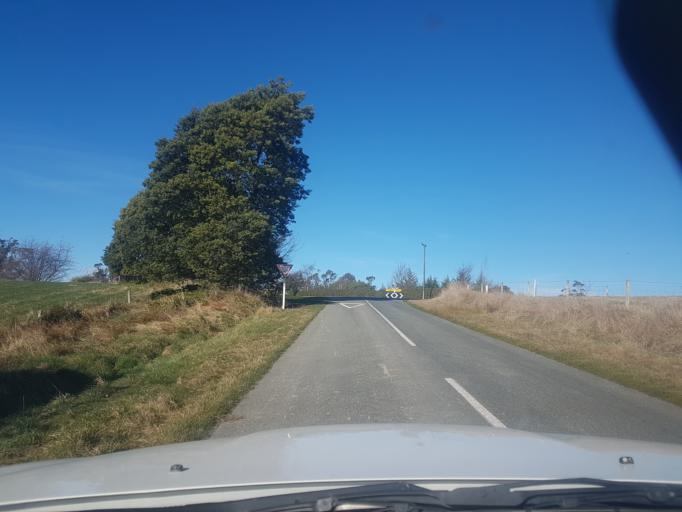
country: NZ
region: Canterbury
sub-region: Timaru District
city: Pleasant Point
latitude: -44.3799
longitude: 171.0907
